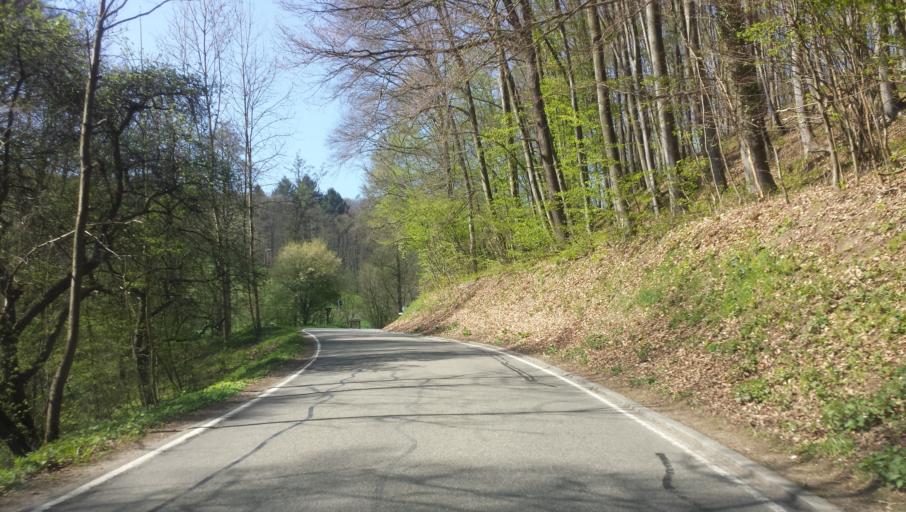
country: DE
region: Hesse
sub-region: Regierungsbezirk Darmstadt
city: Morlenbach
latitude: 49.6250
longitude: 8.7352
